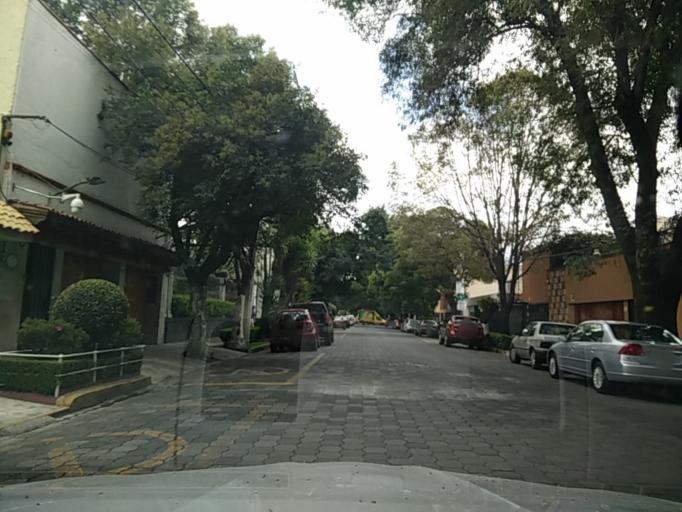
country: MX
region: Mexico City
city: Coyoacan
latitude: 19.3516
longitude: -99.1601
